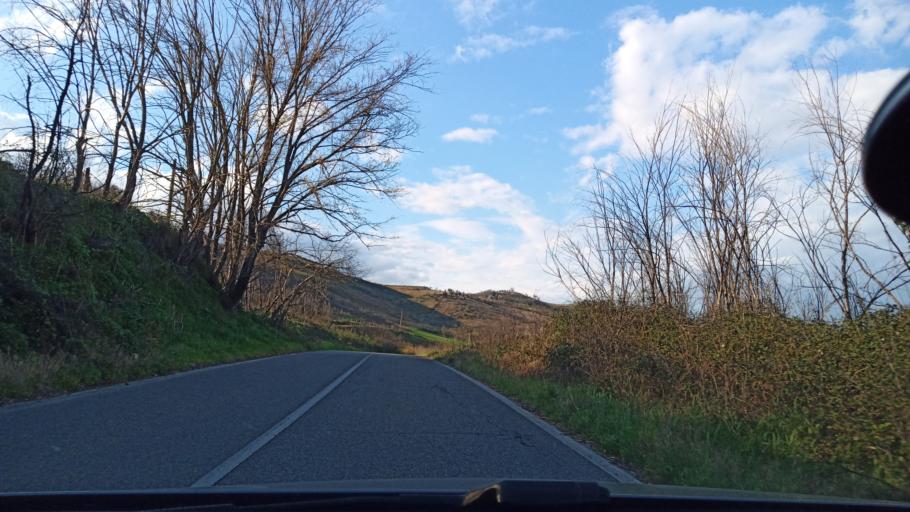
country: IT
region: Latium
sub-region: Citta metropolitana di Roma Capitale
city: Civitella San Paolo
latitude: 42.1872
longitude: 12.6042
